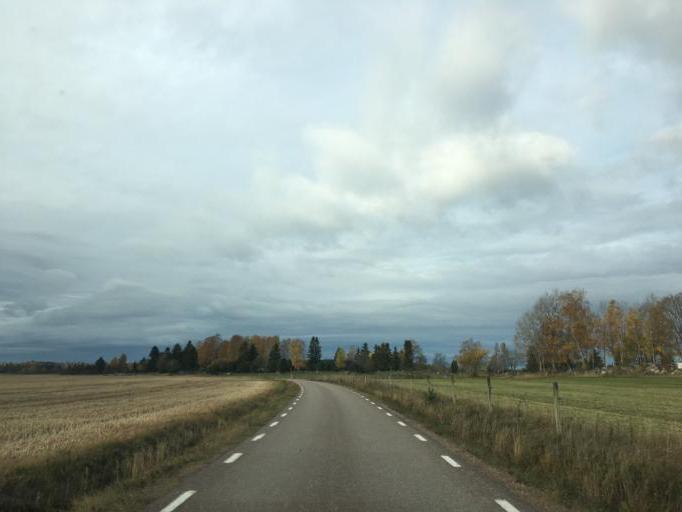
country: SE
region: Soedermanland
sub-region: Eskilstuna Kommun
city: Kvicksund
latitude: 59.5484
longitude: 16.3546
